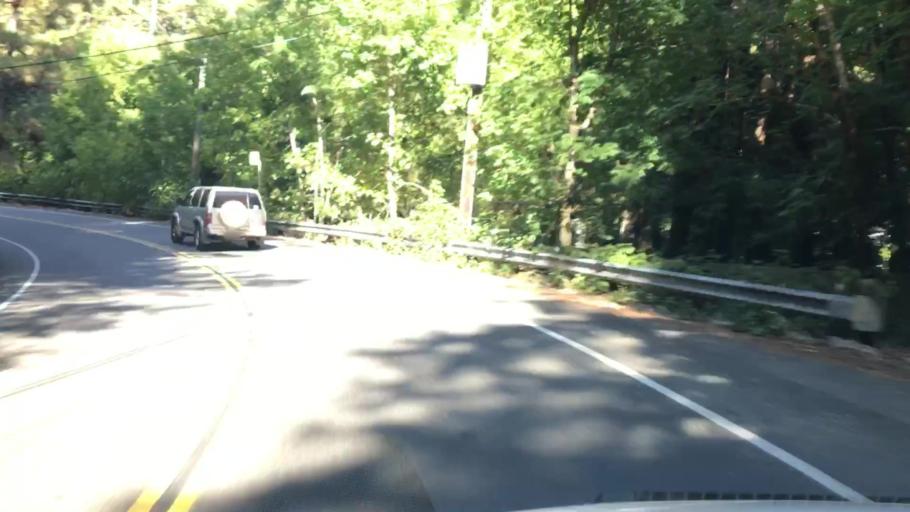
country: US
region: California
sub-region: Marin County
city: Lagunitas-Forest Knolls
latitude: 38.0095
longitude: -122.7023
